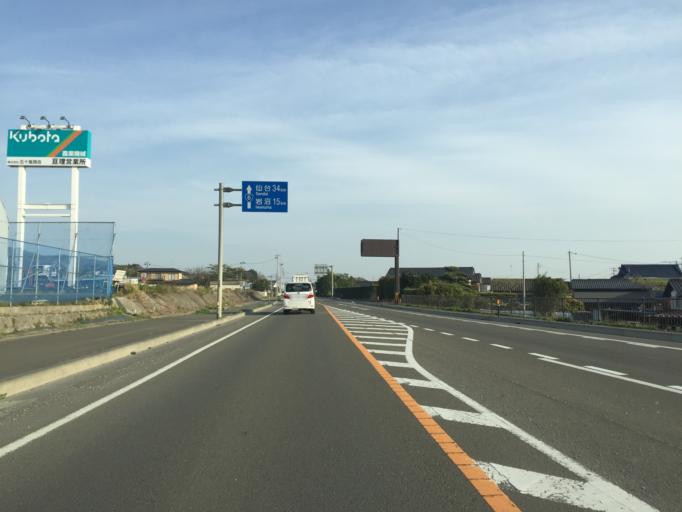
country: JP
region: Miyagi
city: Watari
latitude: 37.9860
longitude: 140.8690
